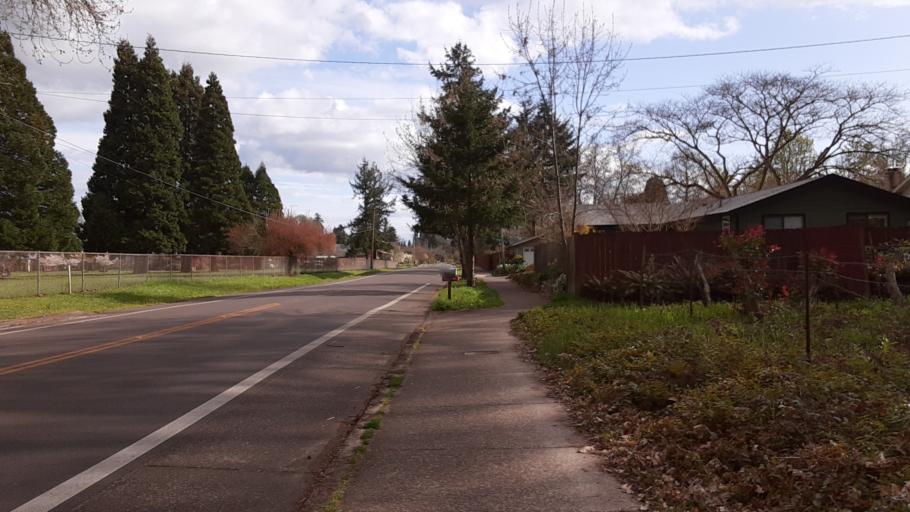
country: US
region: Oregon
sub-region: Benton County
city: Corvallis
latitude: 44.5482
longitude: -123.2558
